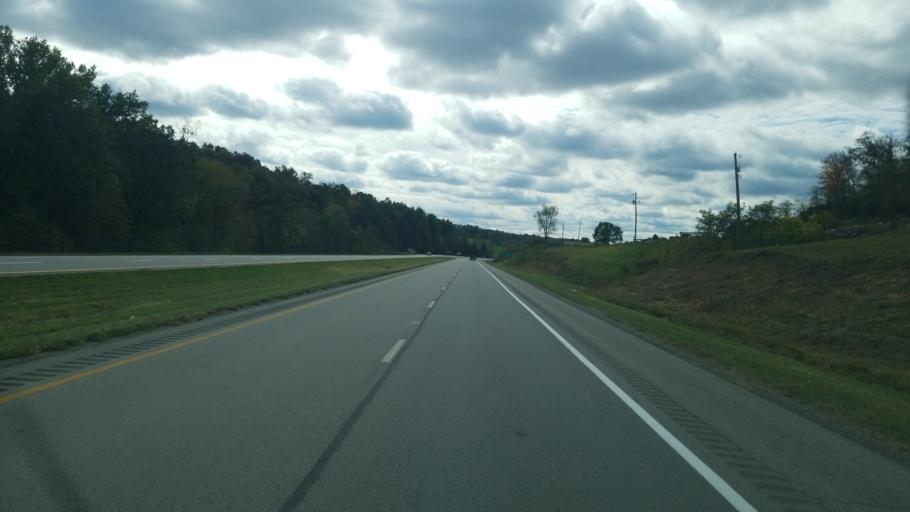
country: US
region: Ohio
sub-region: Jackson County
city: Jackson
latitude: 39.0590
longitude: -82.5890
